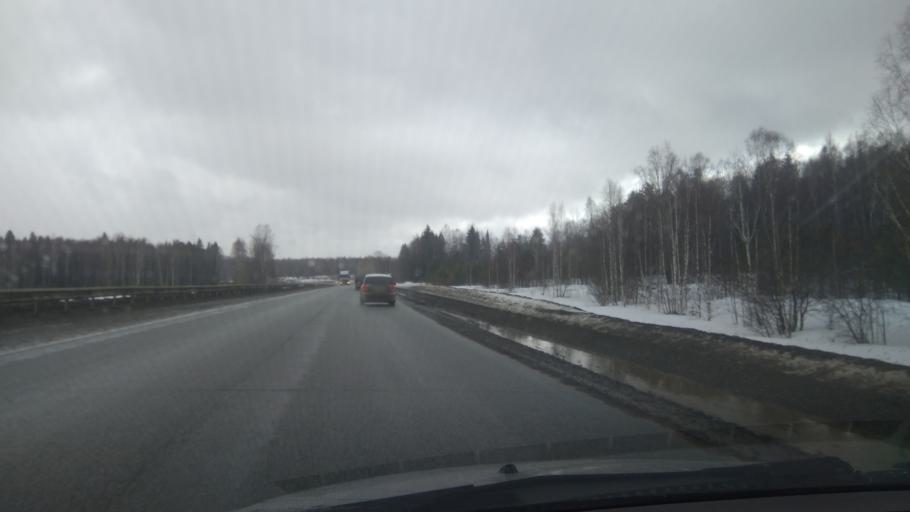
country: RU
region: Sverdlovsk
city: Ufimskiy
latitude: 56.7845
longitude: 58.3937
